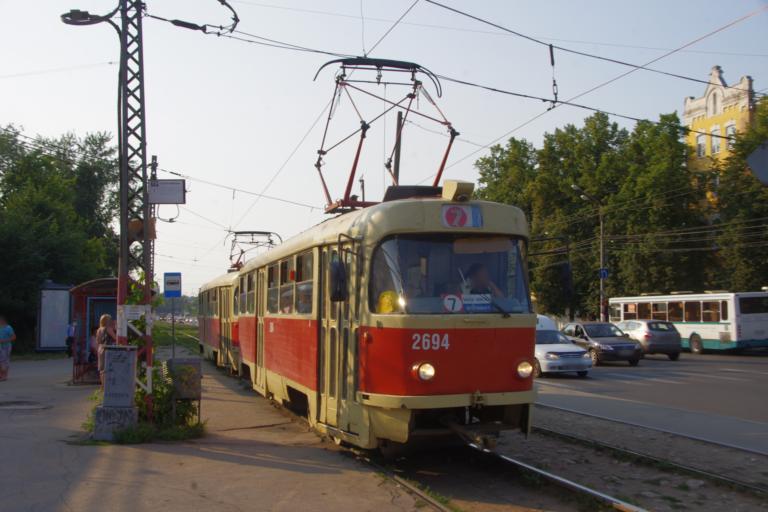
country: RU
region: Nizjnij Novgorod
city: Neklyudovo
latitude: 56.3411
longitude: 43.8784
